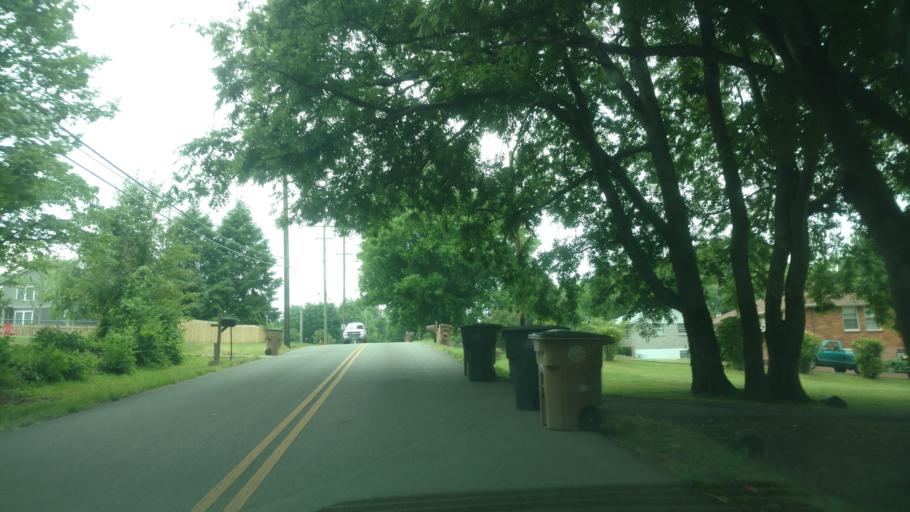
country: US
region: Tennessee
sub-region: Davidson County
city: Nashville
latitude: 36.1957
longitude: -86.7126
